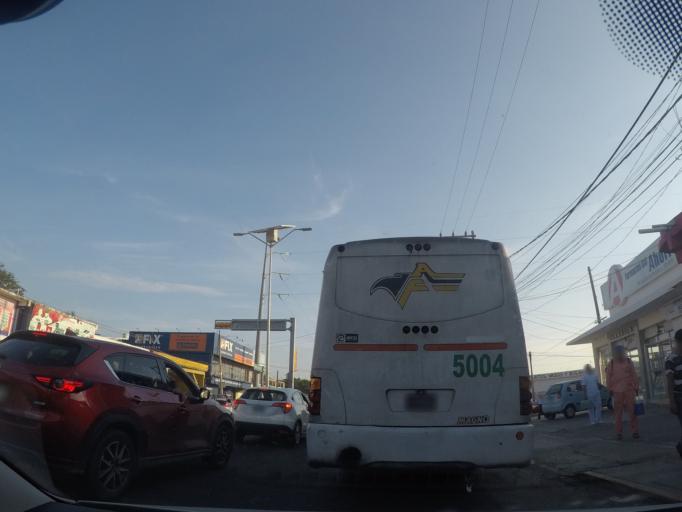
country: MX
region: Oaxaca
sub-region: Salina Cruz
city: Salina Cruz
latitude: 16.1994
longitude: -95.2017
